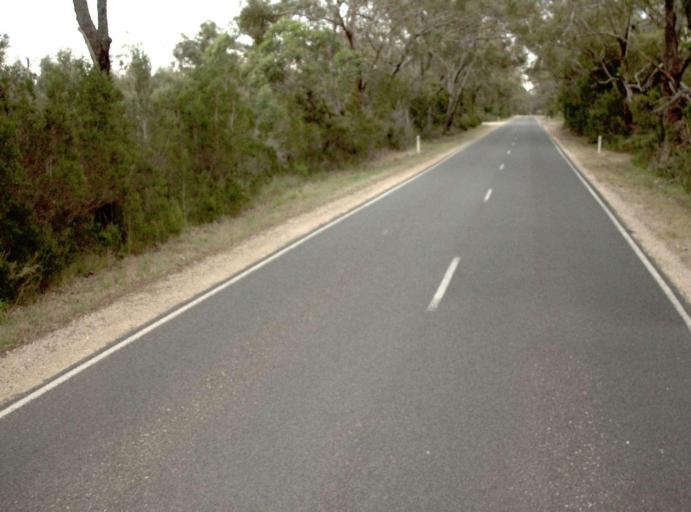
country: AU
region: Victoria
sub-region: Wellington
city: Sale
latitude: -38.1758
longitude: 147.1637
